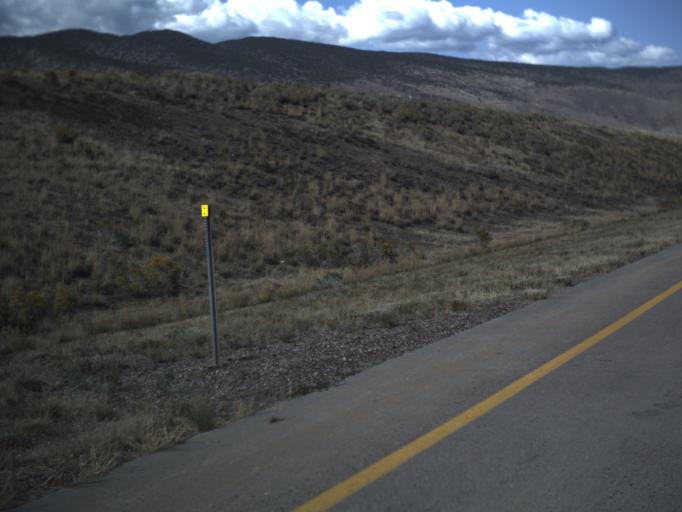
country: US
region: Utah
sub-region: Sevier County
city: Monroe
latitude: 38.6229
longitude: -112.2261
